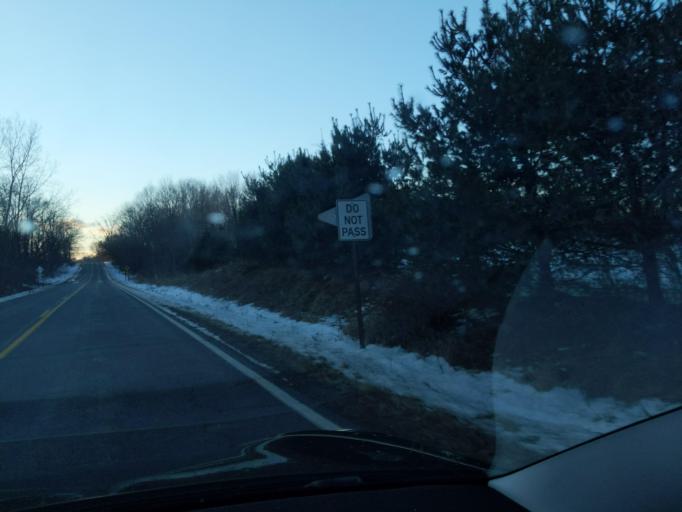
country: US
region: Michigan
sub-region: Ingham County
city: Stockbridge
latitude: 42.4540
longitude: -84.2058
